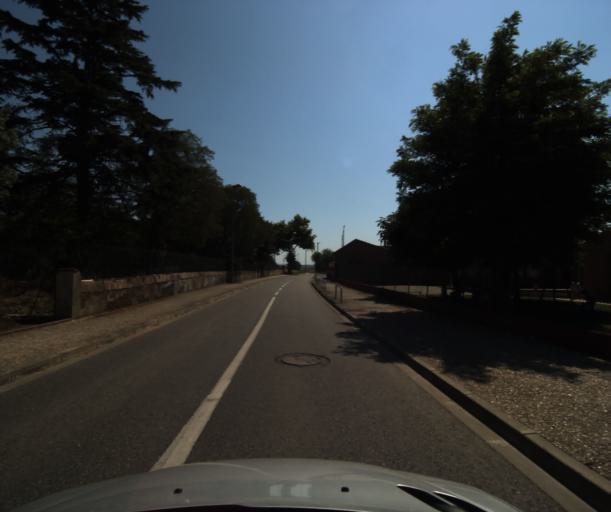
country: FR
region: Midi-Pyrenees
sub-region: Departement de la Haute-Garonne
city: Roquettes
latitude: 43.4771
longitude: 1.3817
